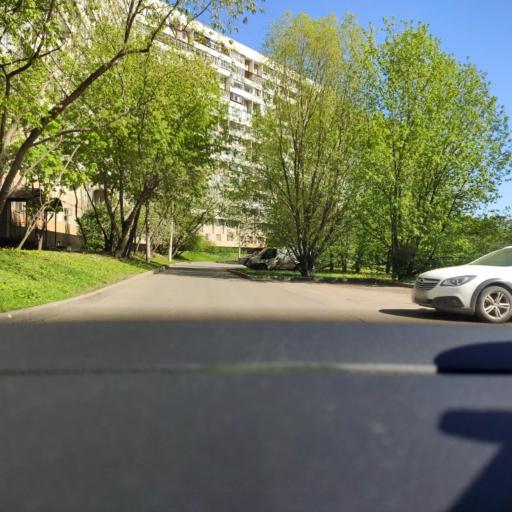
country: RU
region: Moscow
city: Kozeyevo
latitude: 55.8715
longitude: 37.6253
